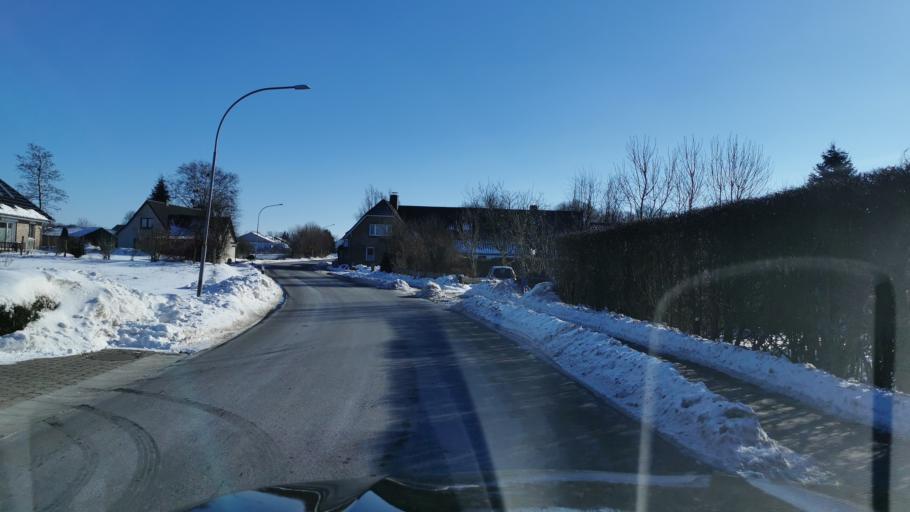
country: DE
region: Schleswig-Holstein
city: Sorup
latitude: 54.7244
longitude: 9.6578
